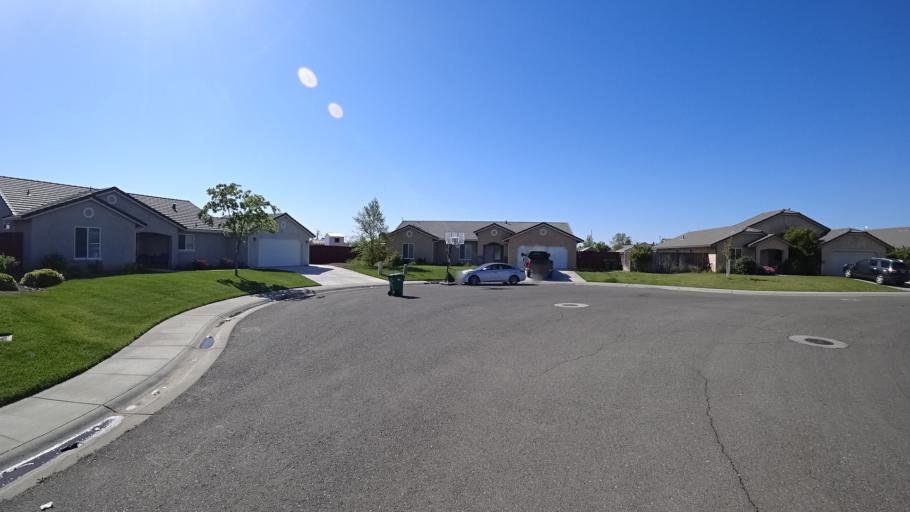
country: US
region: California
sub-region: Glenn County
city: Orland
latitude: 39.7388
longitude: -122.1669
